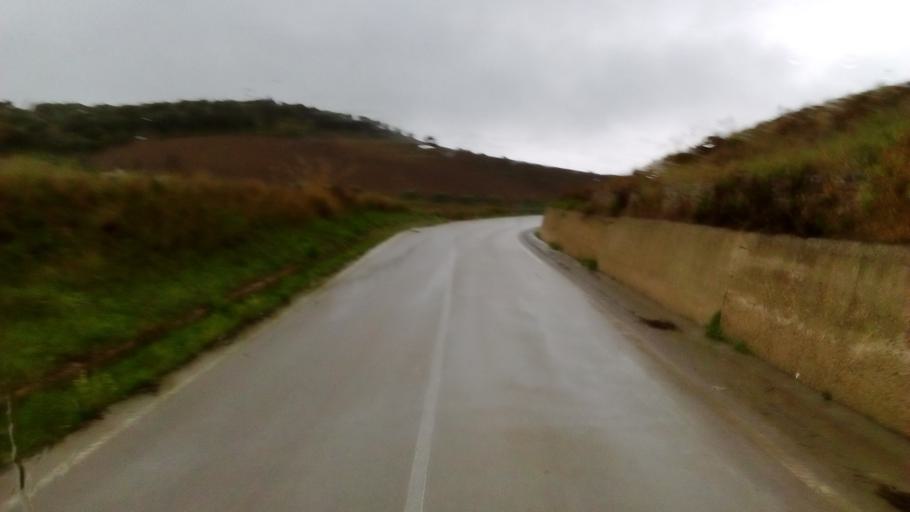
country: IT
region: Sicily
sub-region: Enna
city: Pietraperzia
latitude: 37.4368
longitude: 14.1733
